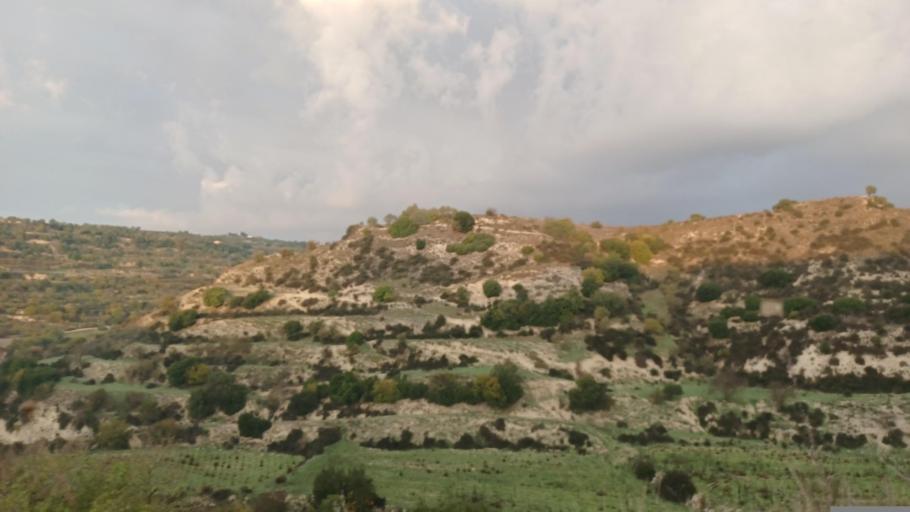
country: CY
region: Pafos
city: Mesogi
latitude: 34.8436
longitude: 32.5197
